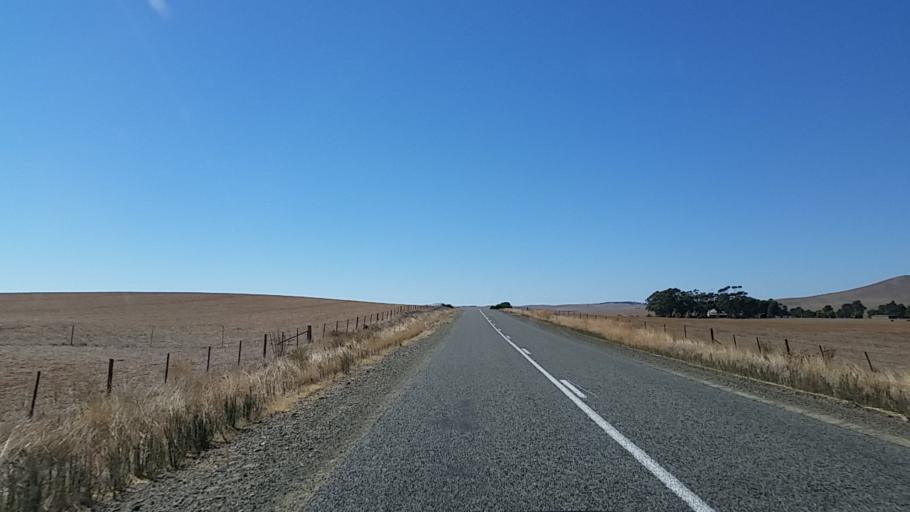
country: AU
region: South Australia
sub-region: Northern Areas
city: Jamestown
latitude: -33.3543
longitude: 138.8882
